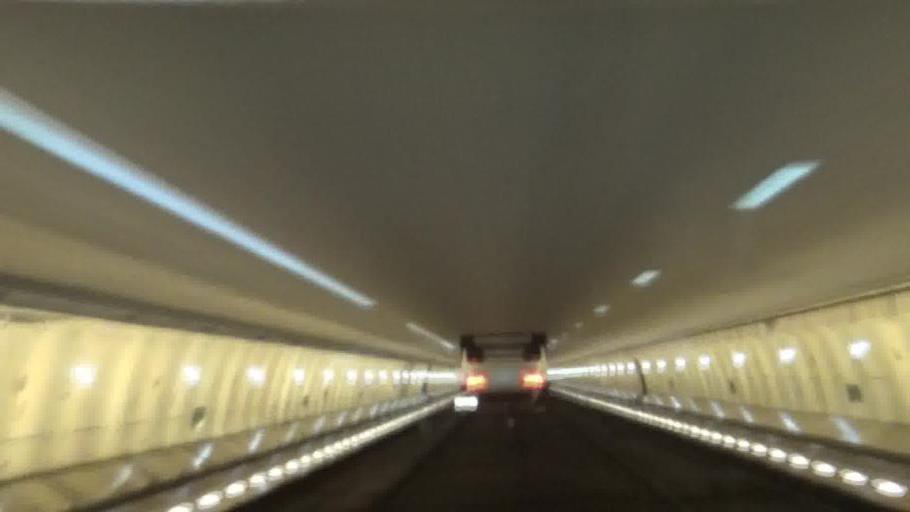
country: FR
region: Ile-de-France
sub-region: Departement des Yvelines
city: Viroflay
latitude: 48.8115
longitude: 2.1603
